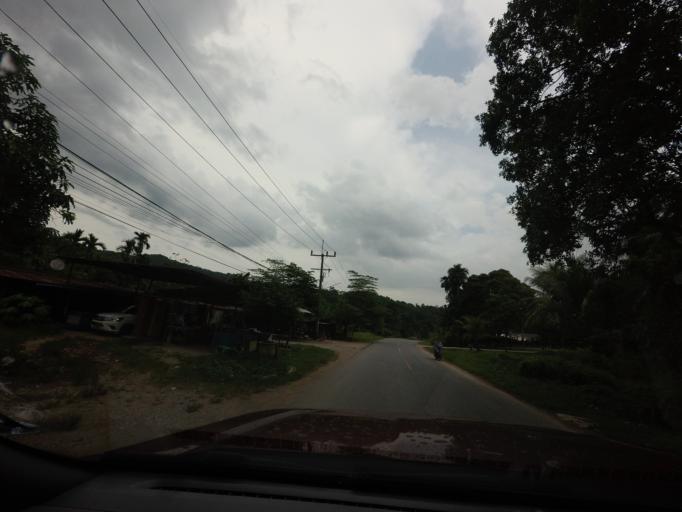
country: TH
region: Yala
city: Than To
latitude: 6.2040
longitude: 101.2367
